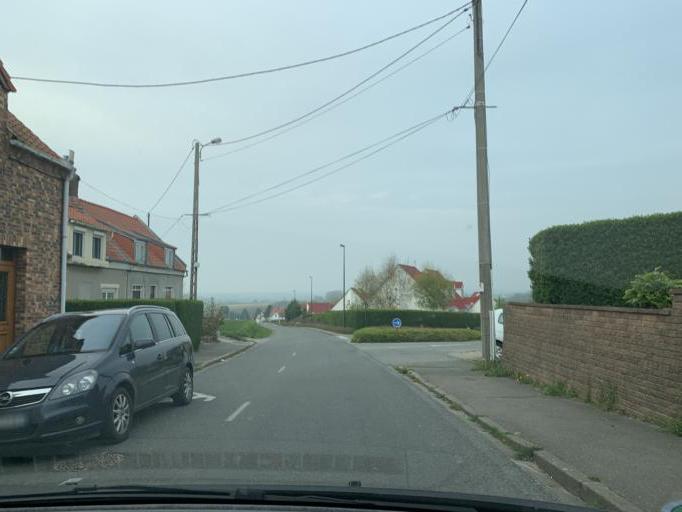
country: FR
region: Nord-Pas-de-Calais
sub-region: Departement du Pas-de-Calais
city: Samer
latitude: 50.6439
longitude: 1.7510
